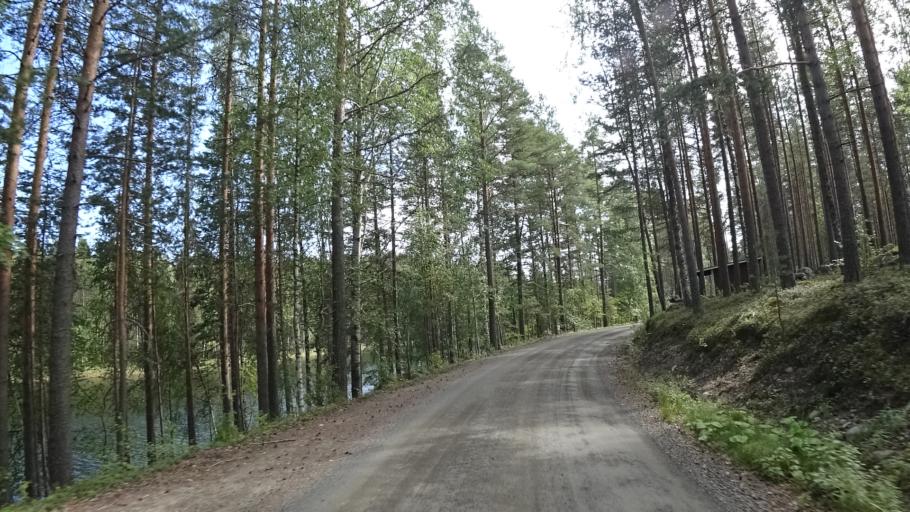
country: FI
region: North Karelia
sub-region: Joensuu
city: Pyhaeselkae
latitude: 62.3817
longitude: 29.8072
